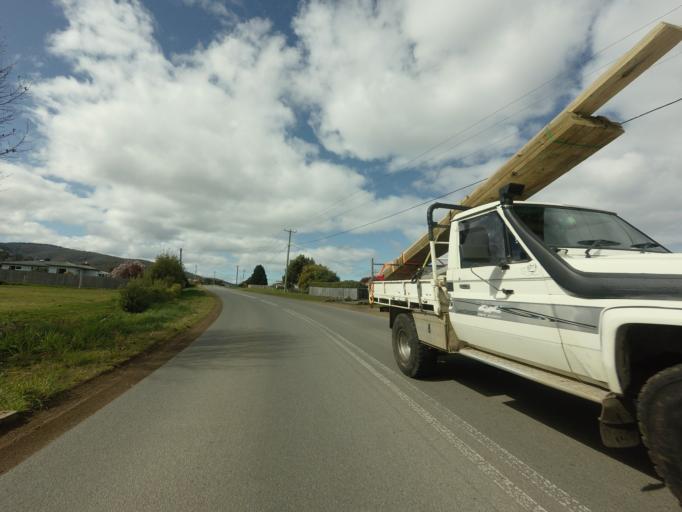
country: AU
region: Tasmania
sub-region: Huon Valley
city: Geeveston
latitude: -43.3222
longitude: 147.0029
